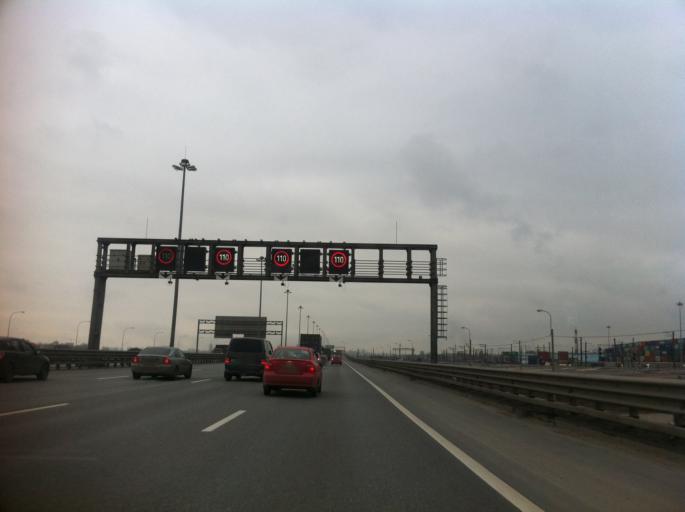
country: RU
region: St.-Petersburg
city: Kupchino
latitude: 59.8171
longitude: 30.3104
